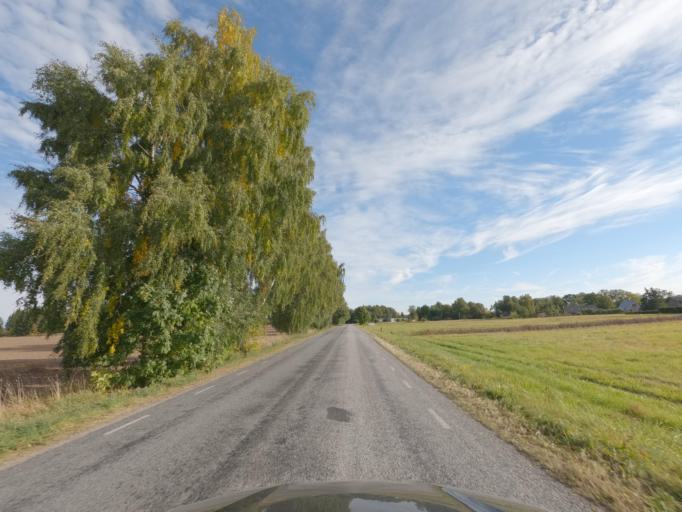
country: EE
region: Raplamaa
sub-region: Rapla vald
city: Rapla
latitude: 59.0526
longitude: 24.6838
